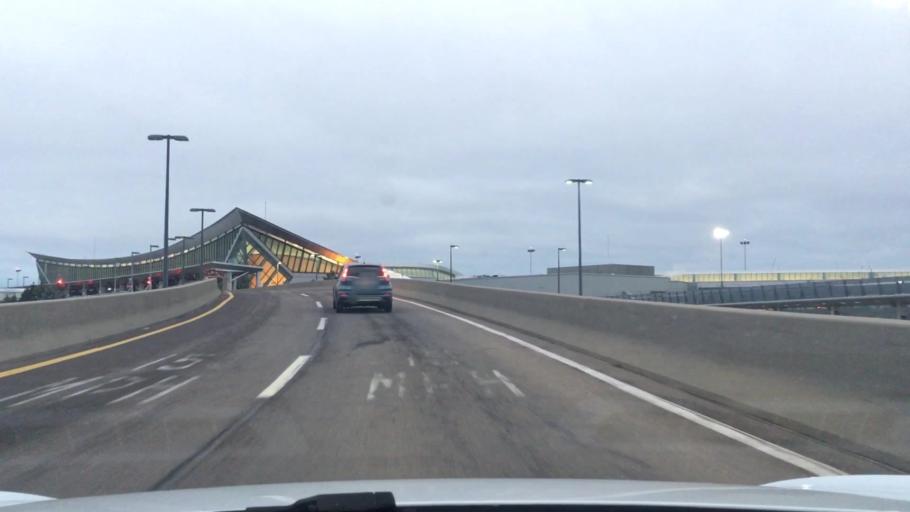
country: US
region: New York
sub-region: Erie County
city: Williamsville
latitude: 42.9340
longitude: -78.7295
